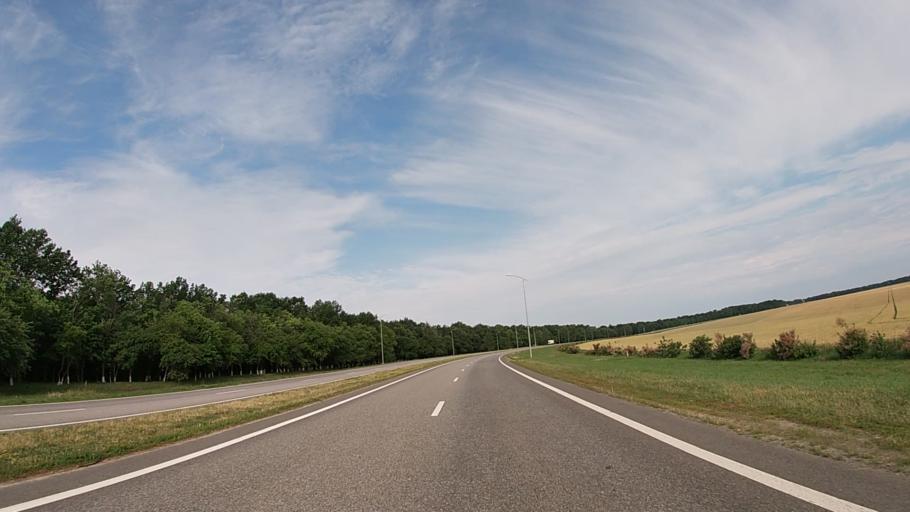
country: RU
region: Belgorod
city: Borisovka
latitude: 50.7514
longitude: 35.9752
